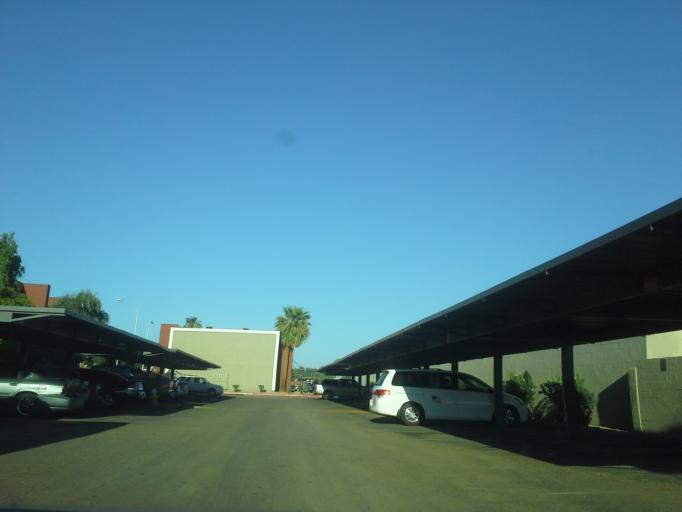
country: US
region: Arizona
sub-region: Maricopa County
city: Glendale
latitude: 33.4993
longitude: -112.1371
